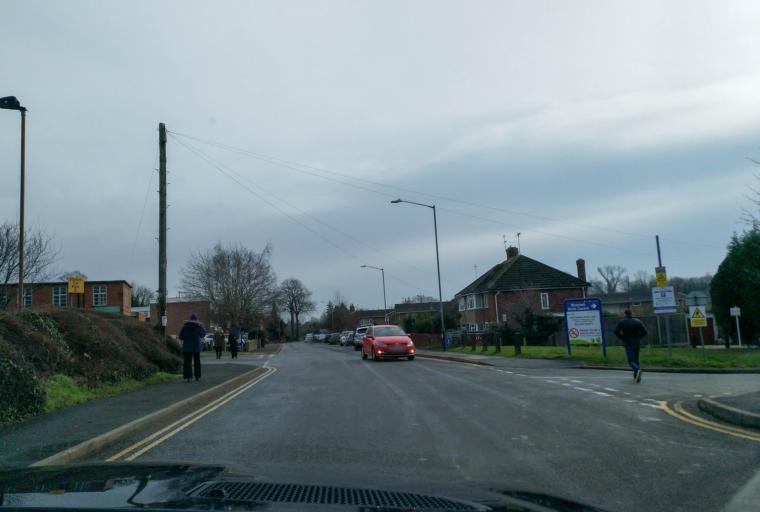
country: GB
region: England
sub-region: Warwickshire
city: Warwick
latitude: 52.2897
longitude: -1.5820
